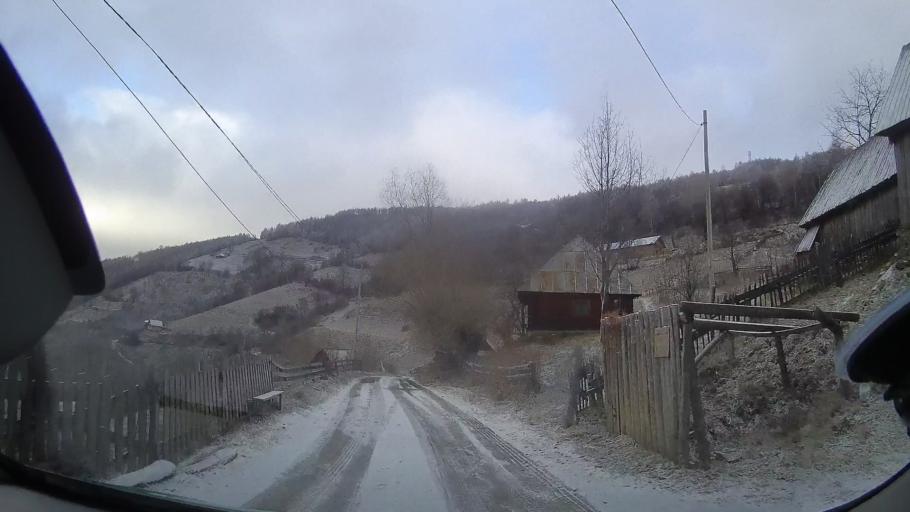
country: RO
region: Cluj
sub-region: Comuna Valea Ierii
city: Valea Ierii
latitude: 46.6665
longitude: 23.3315
